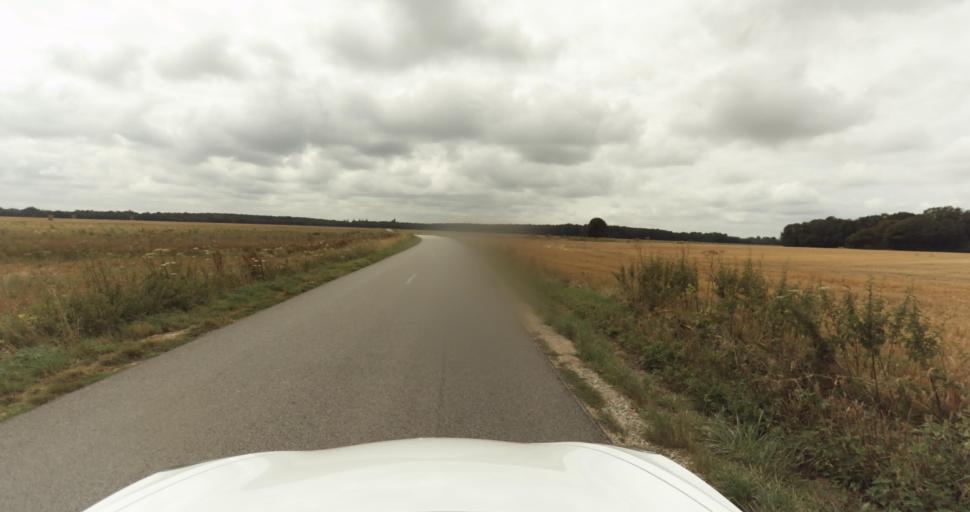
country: FR
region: Haute-Normandie
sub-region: Departement de l'Eure
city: Claville
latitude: 49.0157
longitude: 1.0342
